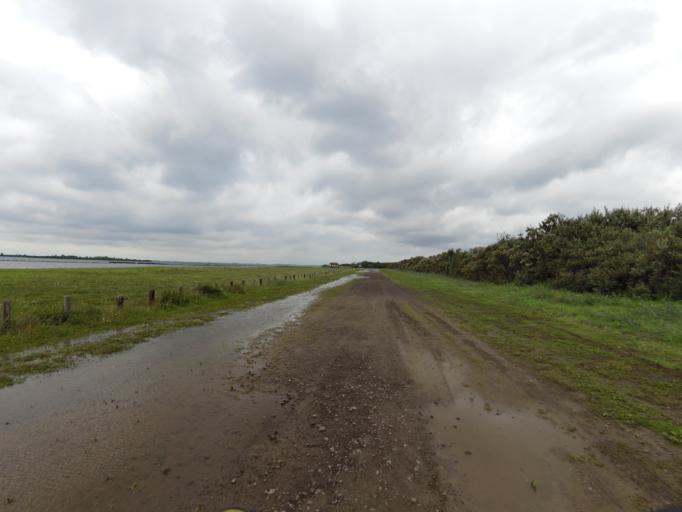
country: NL
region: South Holland
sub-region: Gemeente Goeree-Overflakkee
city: Goedereede
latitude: 51.7508
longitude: 4.0200
